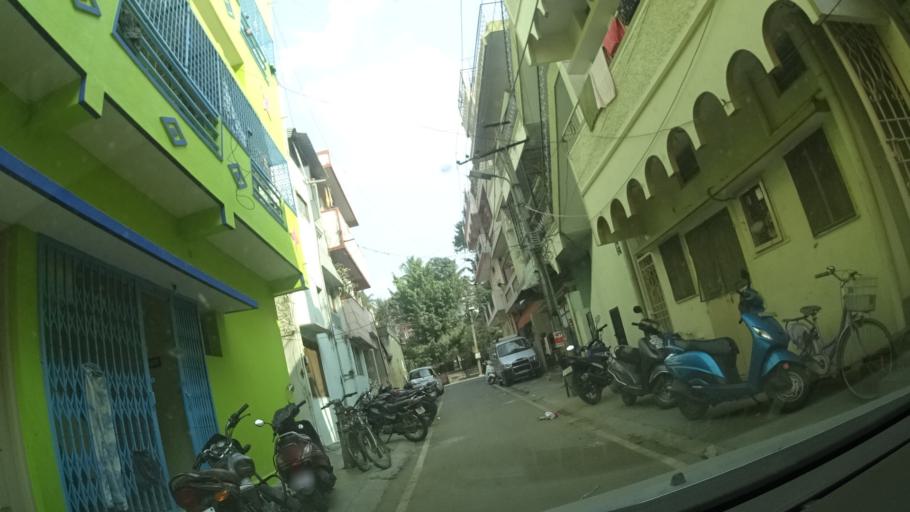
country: IN
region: Karnataka
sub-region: Bangalore Urban
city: Bangalore
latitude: 12.9442
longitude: 77.5672
